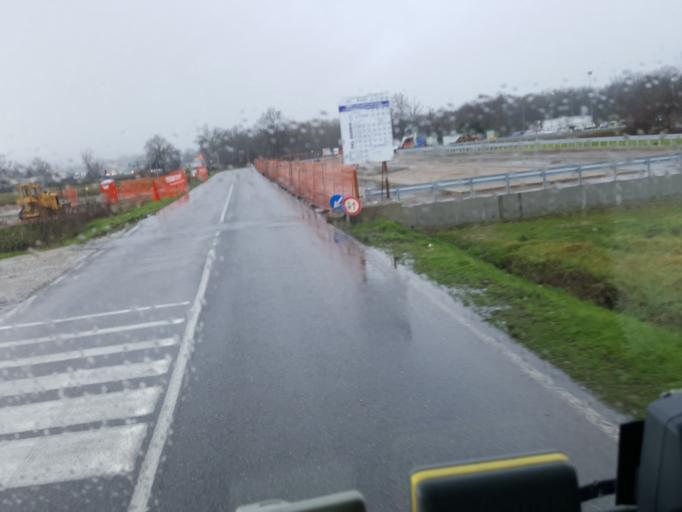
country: IT
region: Tuscany
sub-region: Provincia di Lucca
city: Porcari
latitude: 43.8281
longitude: 10.6052
